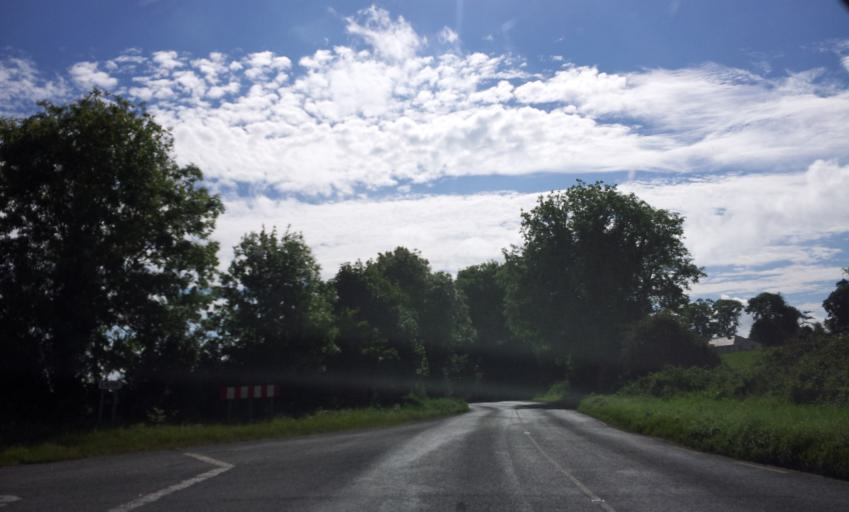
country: IE
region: Leinster
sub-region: Laois
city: Portlaoise
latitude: 53.0110
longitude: -7.2391
